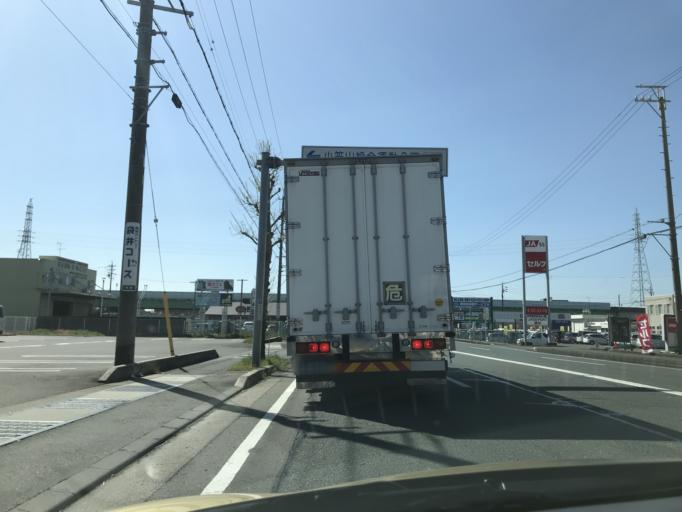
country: JP
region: Shizuoka
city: Fukuroi
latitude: 34.7541
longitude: 137.9077
